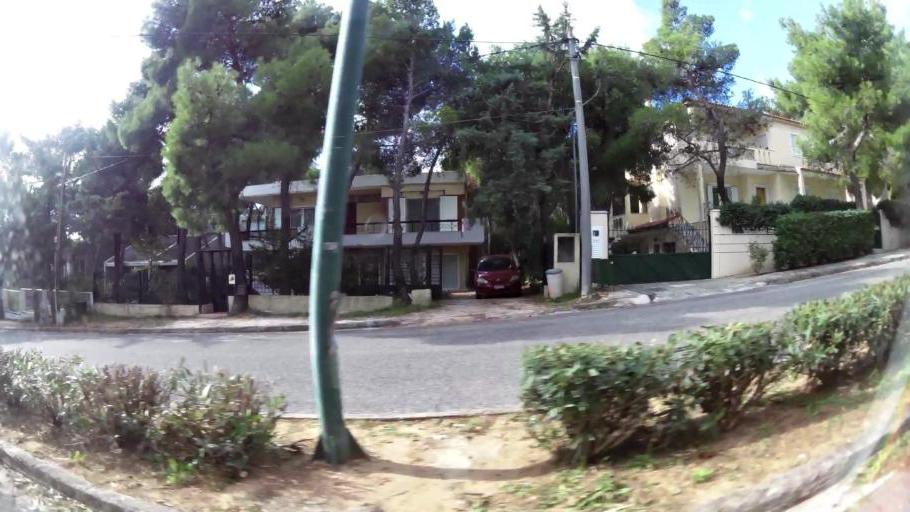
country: GR
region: Attica
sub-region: Nomarchia Anatolikis Attikis
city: Thrakomakedones
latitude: 38.1337
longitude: 23.7619
